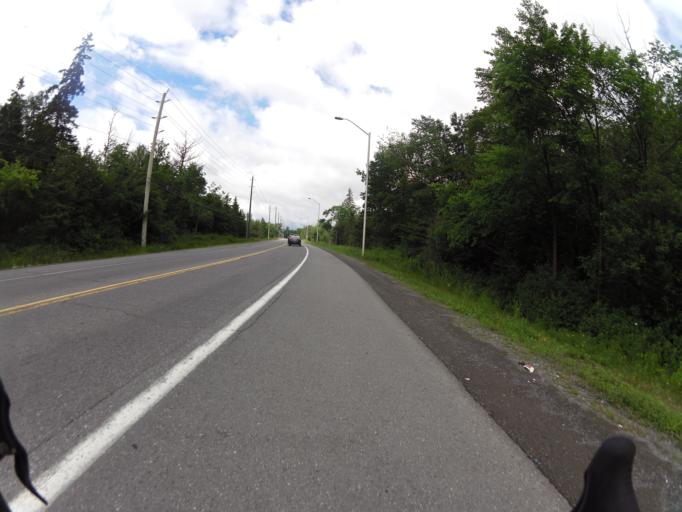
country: CA
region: Ontario
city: Bells Corners
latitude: 45.3033
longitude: -75.8268
